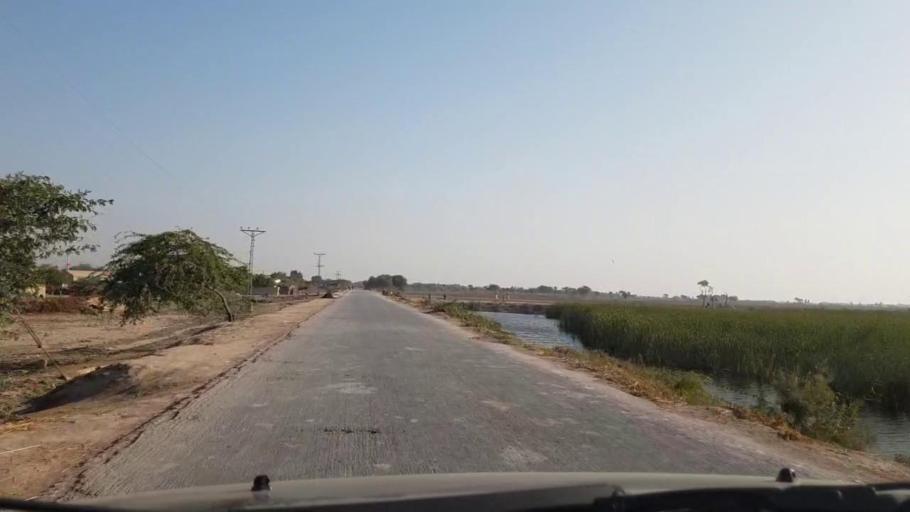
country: PK
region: Sindh
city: Tando Bago
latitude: 24.7959
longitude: 68.9770
